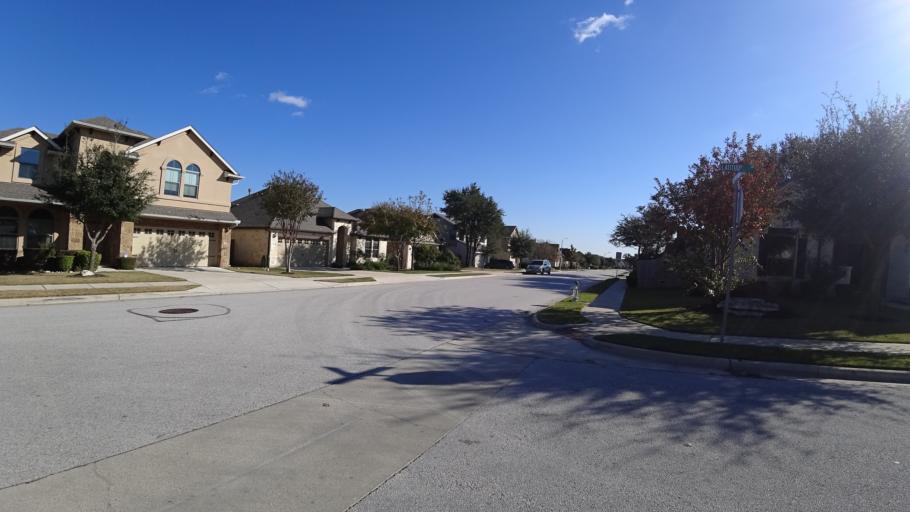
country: US
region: Texas
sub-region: Williamson County
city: Brushy Creek
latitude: 30.4903
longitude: -97.7239
